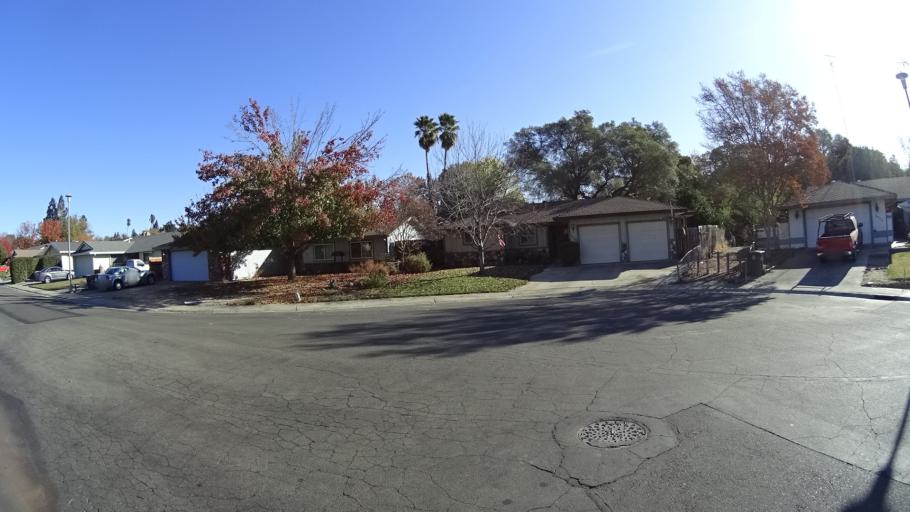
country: US
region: California
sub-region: Sacramento County
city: Citrus Heights
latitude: 38.6748
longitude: -121.3000
